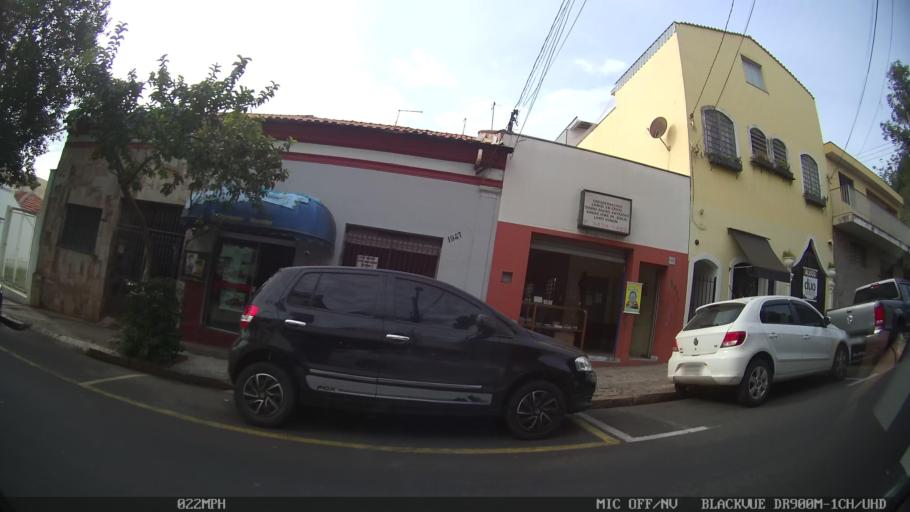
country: BR
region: Sao Paulo
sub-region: Piracicaba
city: Piracicaba
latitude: -22.7300
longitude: -47.6390
